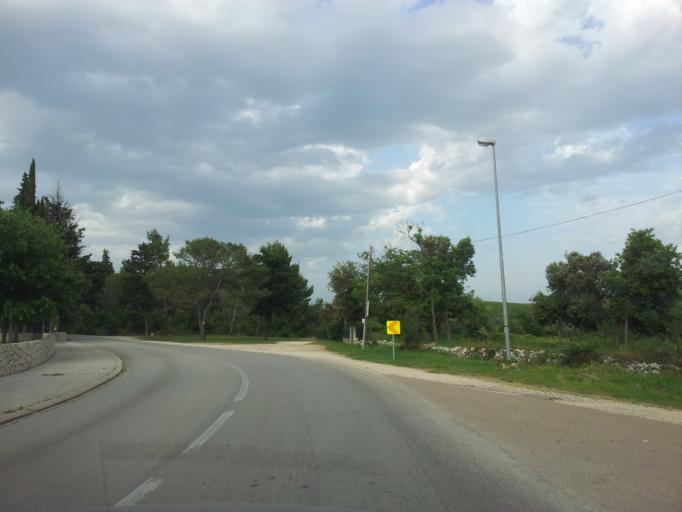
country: HR
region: Zadarska
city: Sukosan
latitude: 44.0480
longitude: 15.3260
